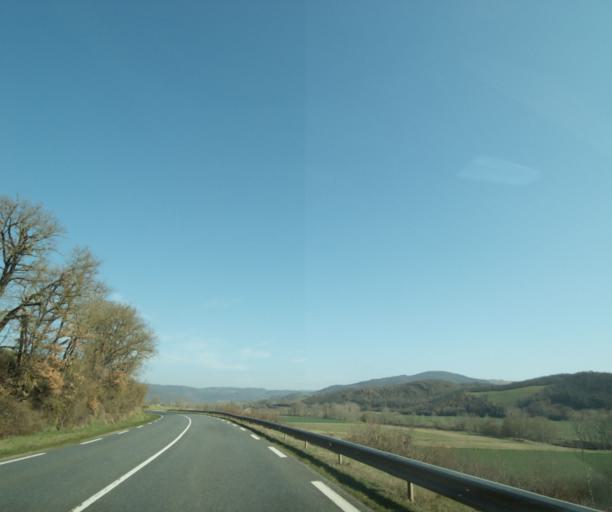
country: FR
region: Midi-Pyrenees
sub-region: Departement de l'Aveyron
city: Saint-Affrique
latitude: 43.9135
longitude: 2.8251
